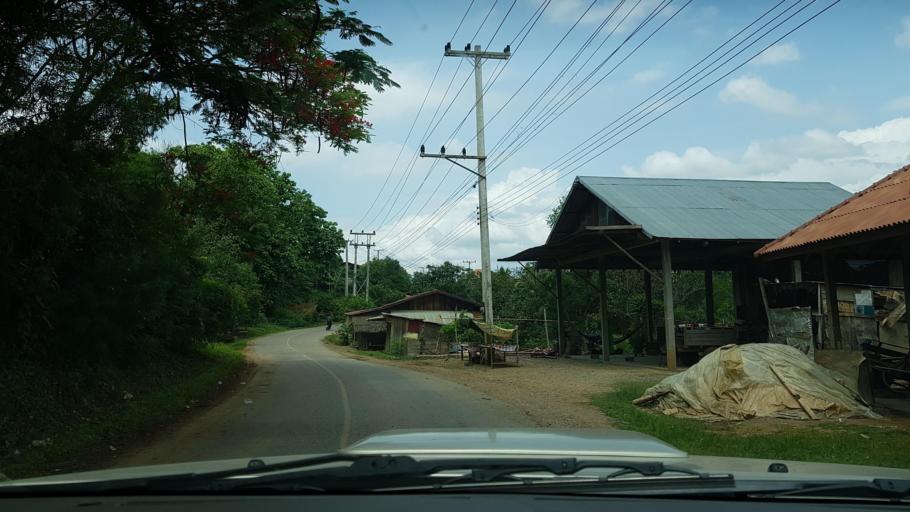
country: TH
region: Nan
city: Chaloem Phra Kiat
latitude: 20.0114
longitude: 101.3140
